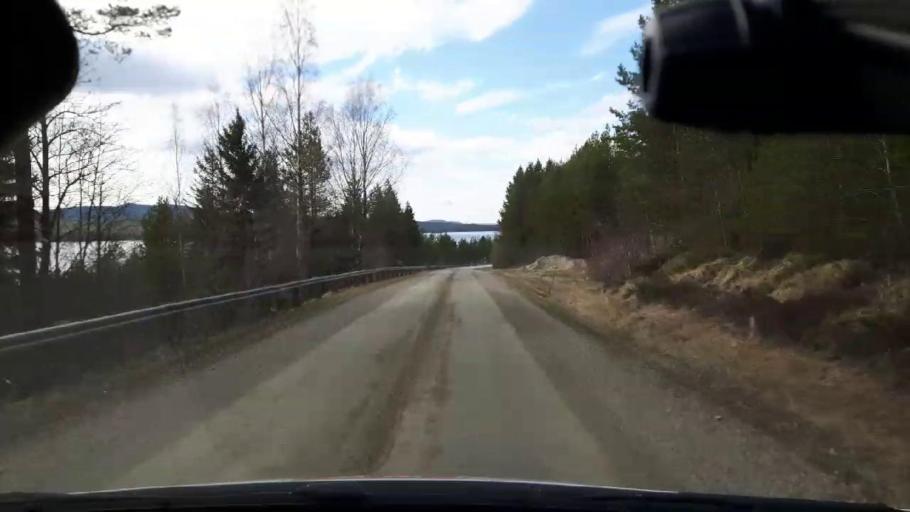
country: SE
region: Jaemtland
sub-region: Bergs Kommun
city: Hoverberg
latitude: 62.7222
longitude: 14.6723
